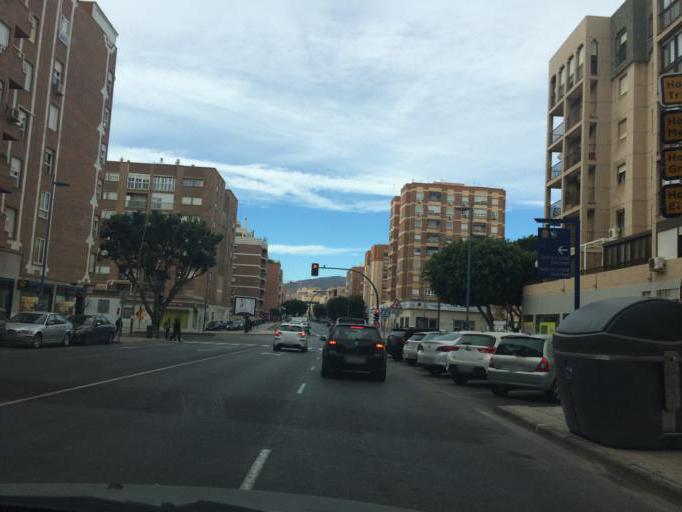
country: ES
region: Andalusia
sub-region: Provincia de Almeria
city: Almeria
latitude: 36.8433
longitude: -2.4465
